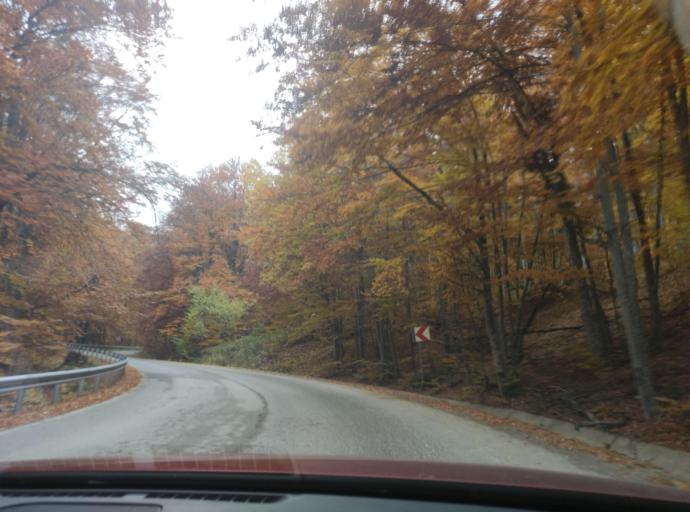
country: BG
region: Montana
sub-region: Obshtina Berkovitsa
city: Berkovitsa
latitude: 43.1185
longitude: 23.1200
